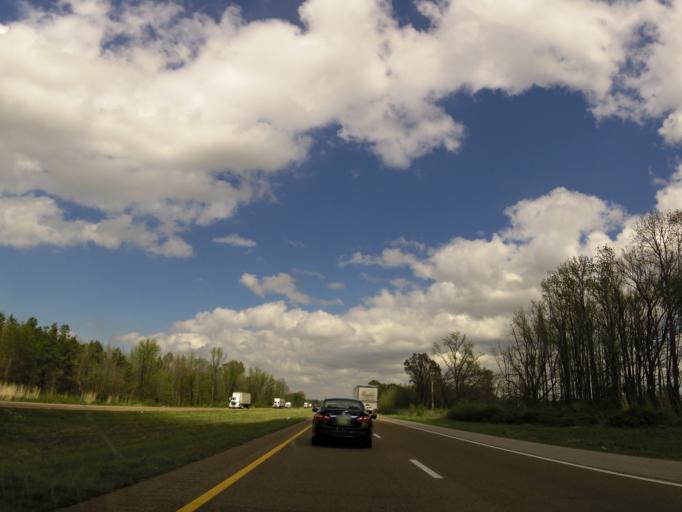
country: US
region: Tennessee
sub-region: Fayette County
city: Hickory Withe
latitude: 35.3069
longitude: -89.5892
